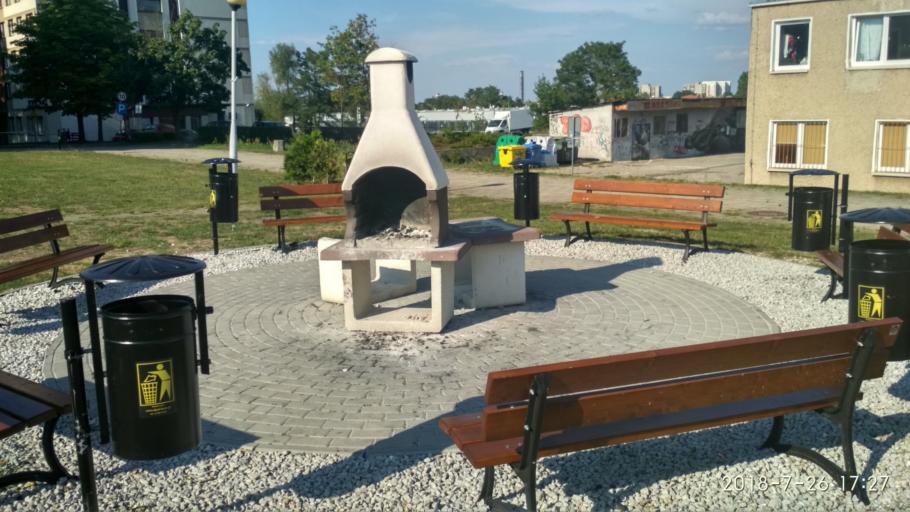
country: PL
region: Lubusz
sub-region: Zielona Gora
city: Zielona Gora
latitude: 51.9403
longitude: 15.4741
